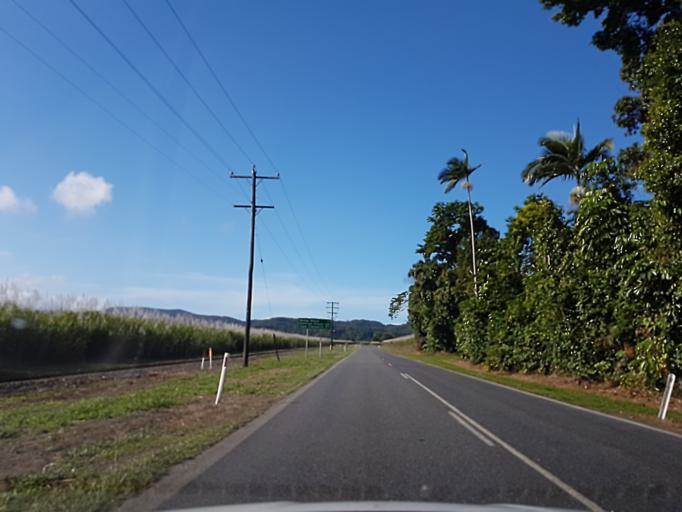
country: AU
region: Queensland
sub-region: Cairns
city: Port Douglas
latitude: -16.3986
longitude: 145.3824
